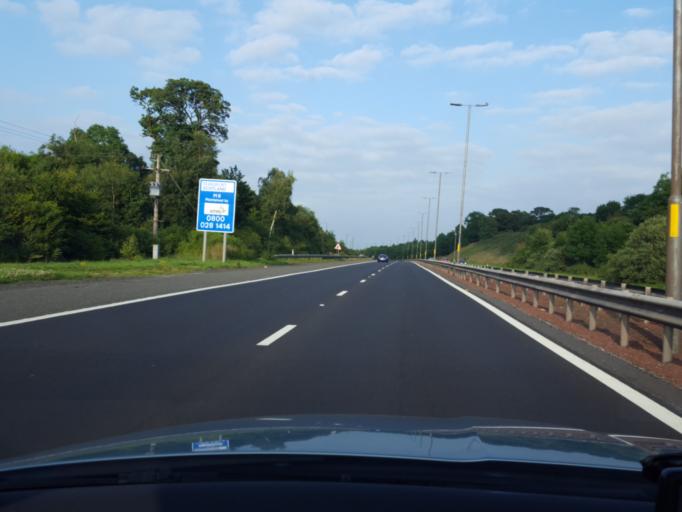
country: GB
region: Scotland
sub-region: Edinburgh
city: Newbridge
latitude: 55.9261
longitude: -3.4004
